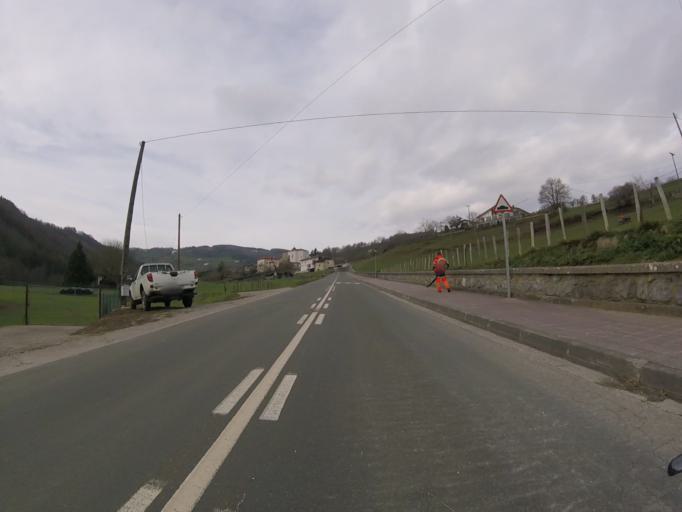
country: ES
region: Basque Country
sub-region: Provincia de Guipuzcoa
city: Errezil
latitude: 43.1414
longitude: -2.1644
